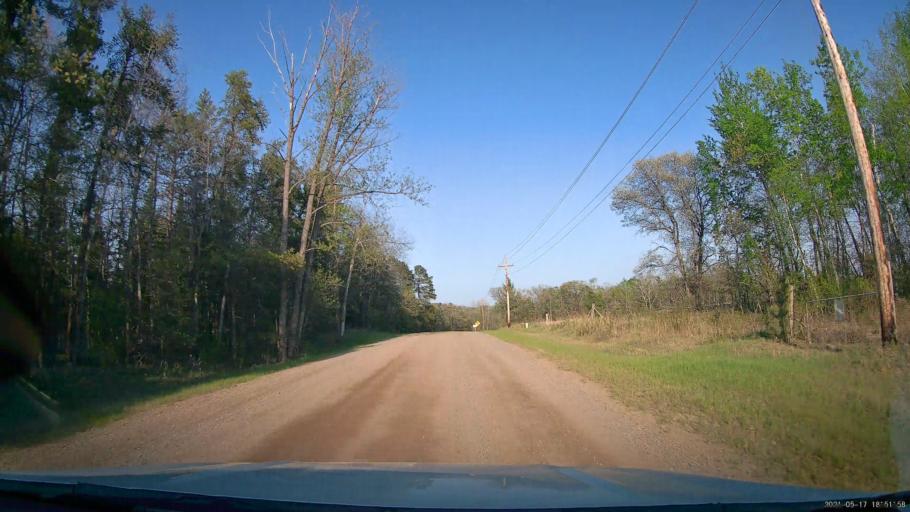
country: US
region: Minnesota
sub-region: Hubbard County
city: Park Rapids
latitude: 46.9438
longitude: -95.0056
